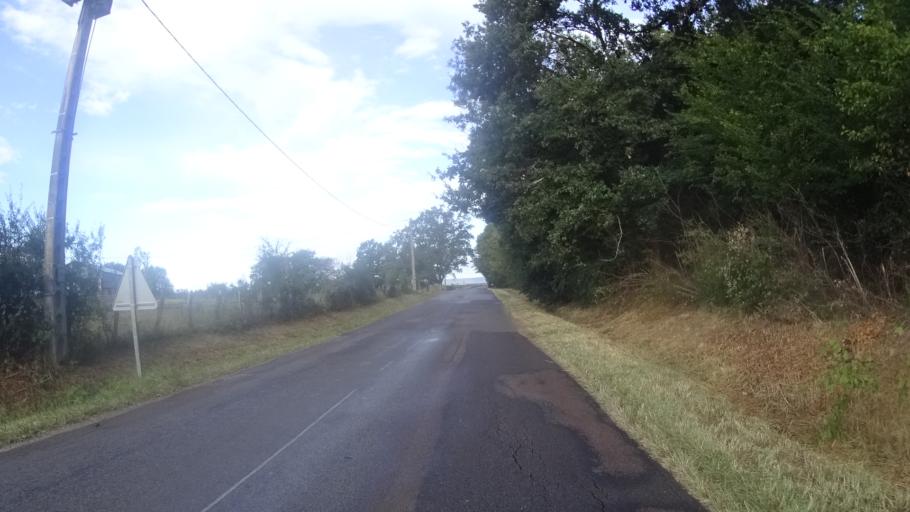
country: FR
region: Bourgogne
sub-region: Departement de Saone-et-Loire
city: Demigny
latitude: 46.9575
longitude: 4.8900
